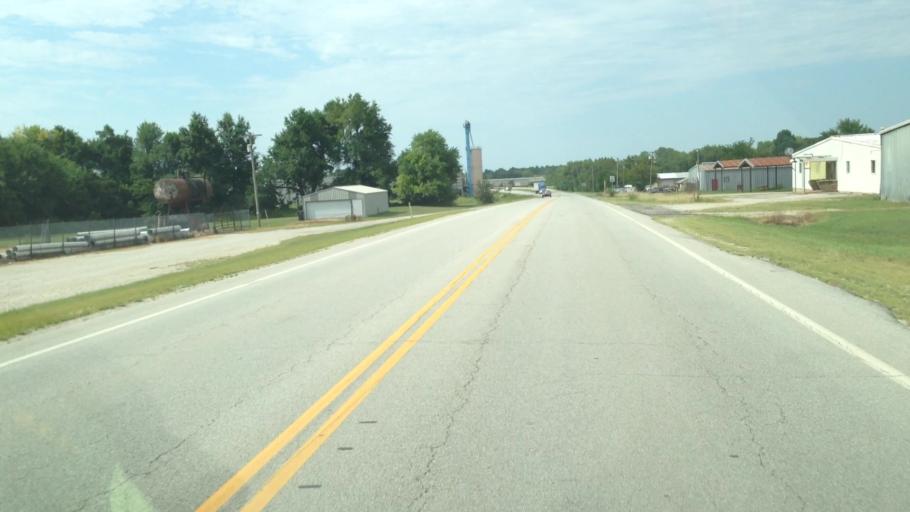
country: US
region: Kansas
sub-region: Labette County
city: Chetopa
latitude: 37.0431
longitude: -95.1002
